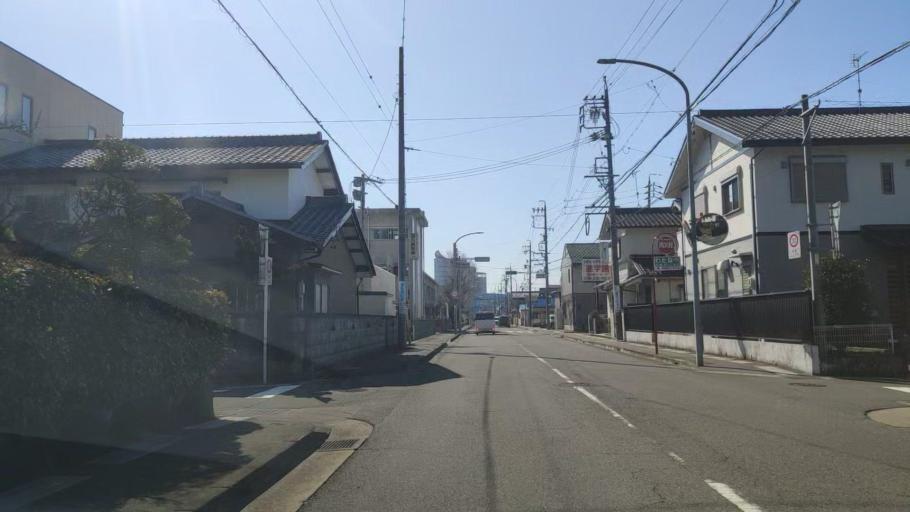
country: JP
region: Gifu
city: Gifu-shi
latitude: 35.4461
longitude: 136.7690
